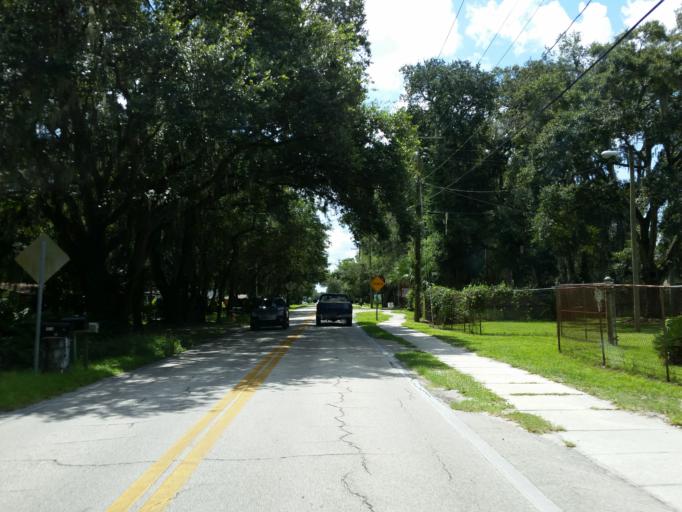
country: US
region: Florida
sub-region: Hillsborough County
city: Riverview
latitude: 27.8832
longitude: -82.3309
